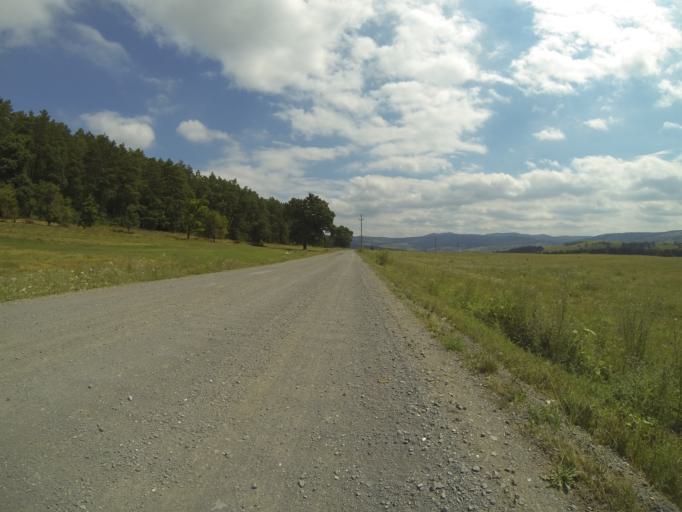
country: RO
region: Brasov
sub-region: Comuna Hoghiz
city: Hoghiz
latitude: 45.9779
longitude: 25.3397
